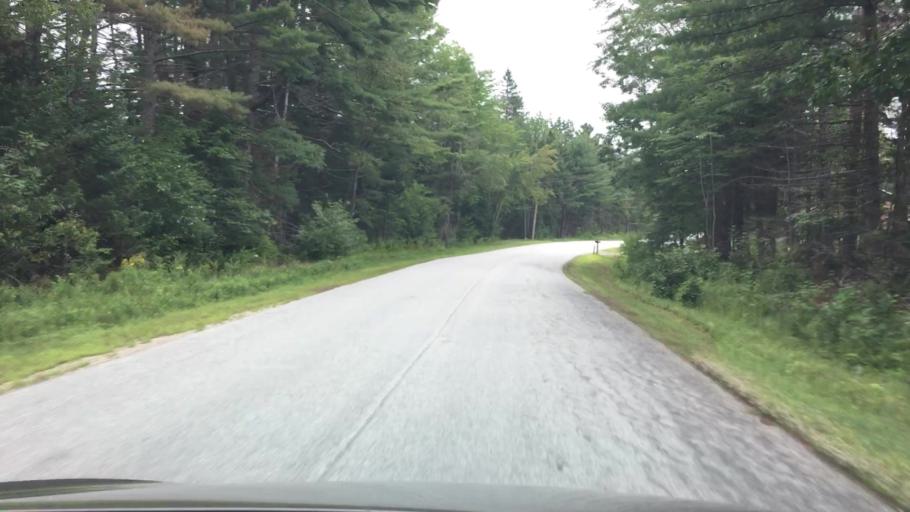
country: US
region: Maine
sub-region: Waldo County
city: Stockton Springs
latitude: 44.5293
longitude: -68.8324
